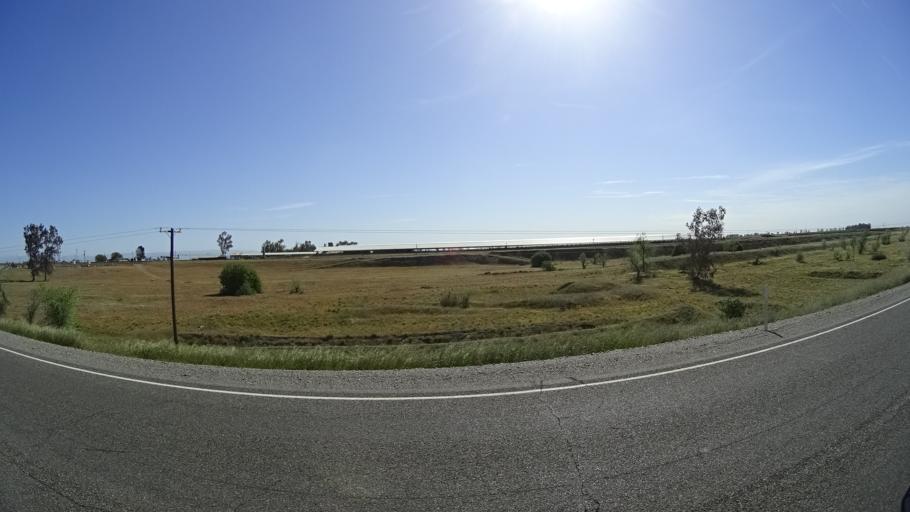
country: US
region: California
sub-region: Glenn County
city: Orland
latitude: 39.6800
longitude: -122.1971
